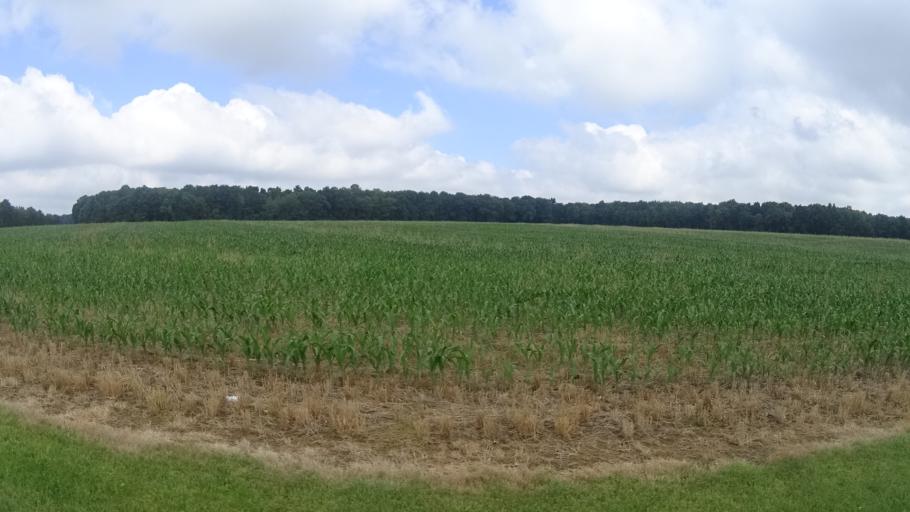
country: US
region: Ohio
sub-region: Huron County
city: Wakeman
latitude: 41.2952
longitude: -82.4188
